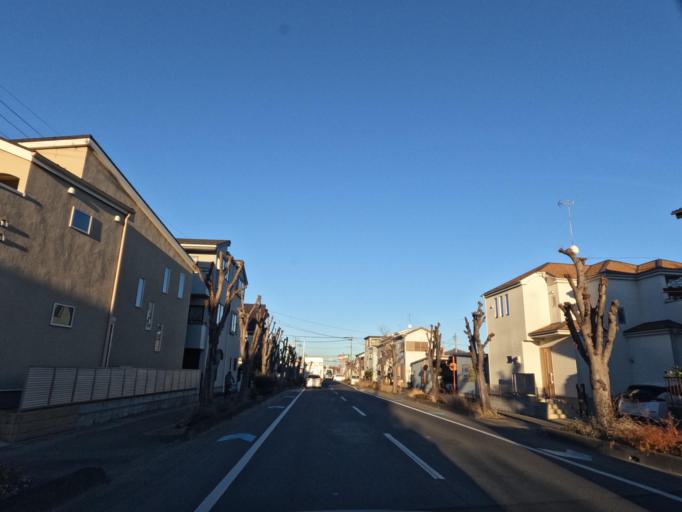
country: JP
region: Saitama
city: Iwatsuki
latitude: 35.9609
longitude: 139.6867
